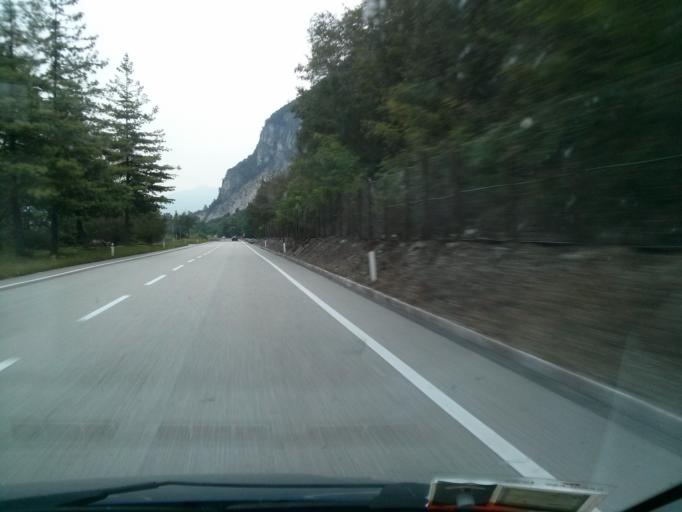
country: IT
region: Trentino-Alto Adige
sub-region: Provincia di Trento
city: Besenello
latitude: 45.9651
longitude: 11.1121
